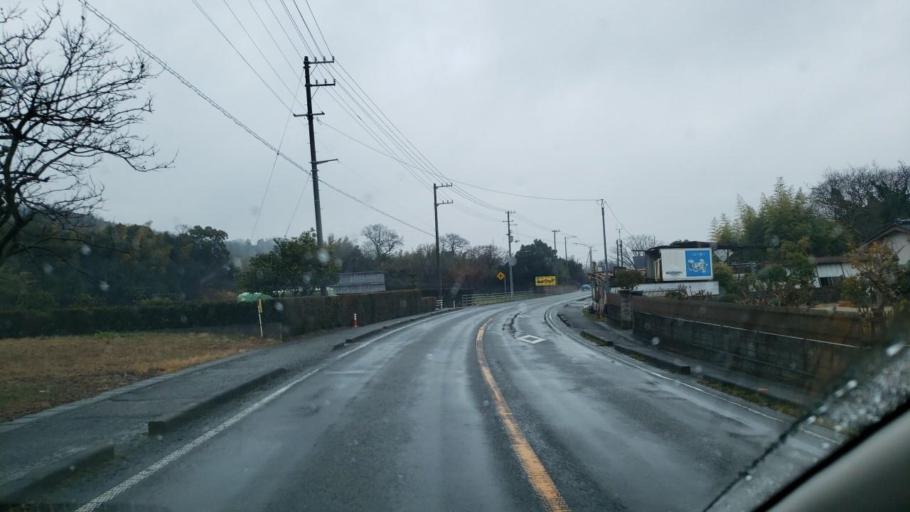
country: JP
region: Tokushima
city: Tokushima-shi
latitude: 34.1567
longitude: 134.5151
